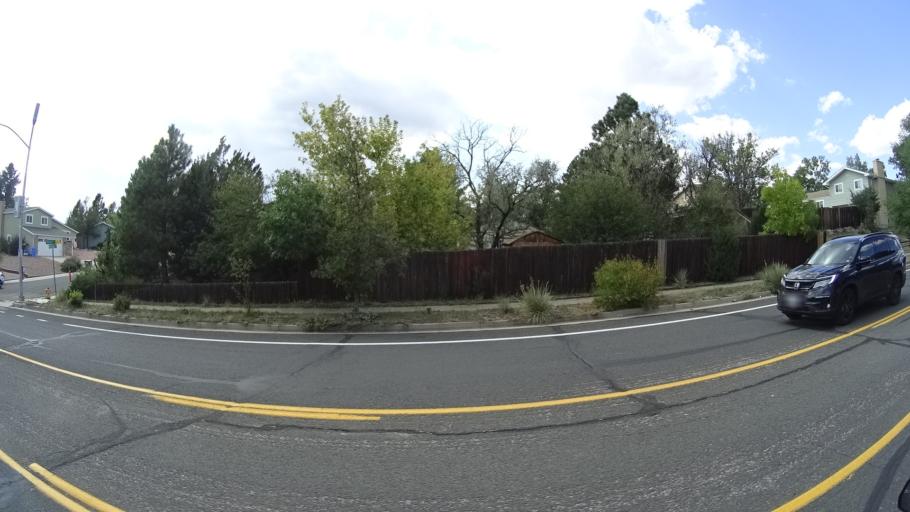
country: US
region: Colorado
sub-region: El Paso County
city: Cimarron Hills
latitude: 38.8728
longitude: -104.7232
